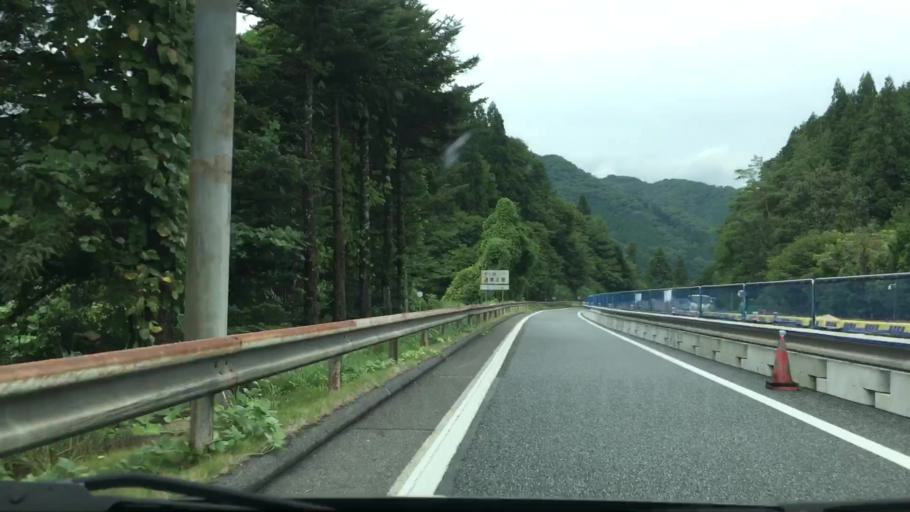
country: JP
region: Okayama
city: Niimi
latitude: 35.0202
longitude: 133.5817
